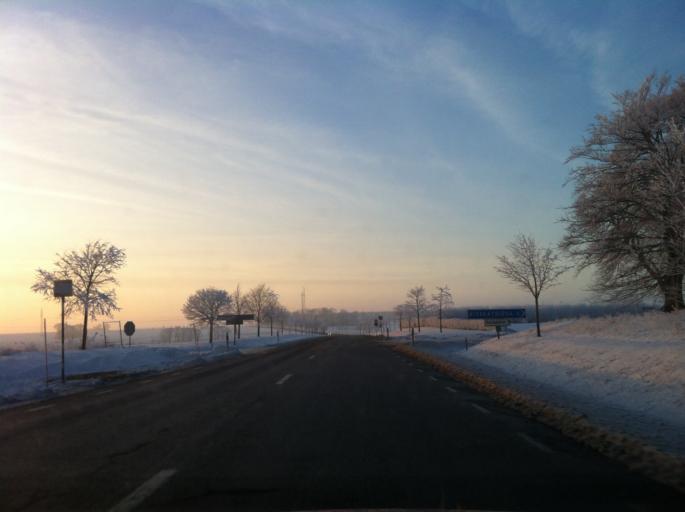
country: SE
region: Skane
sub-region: Bjuvs Kommun
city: Billesholm
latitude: 56.0503
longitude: 12.9994
